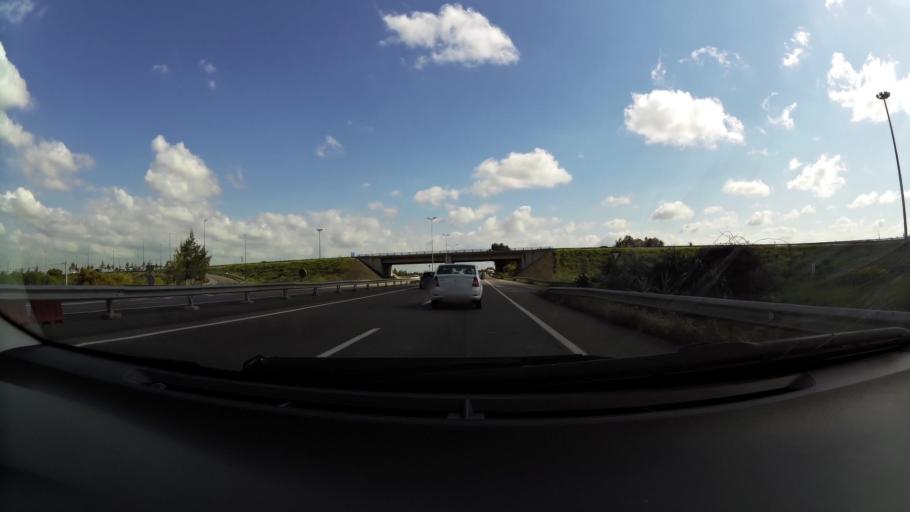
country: MA
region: Chaouia-Ouardigha
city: Nouaseur
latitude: 33.3914
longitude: -7.6198
